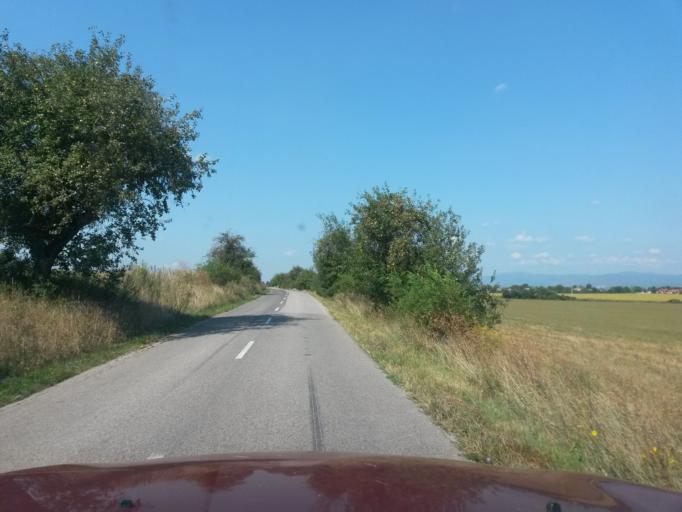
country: SK
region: Kosicky
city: Moldava nad Bodvou
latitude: 48.5315
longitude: 21.1212
